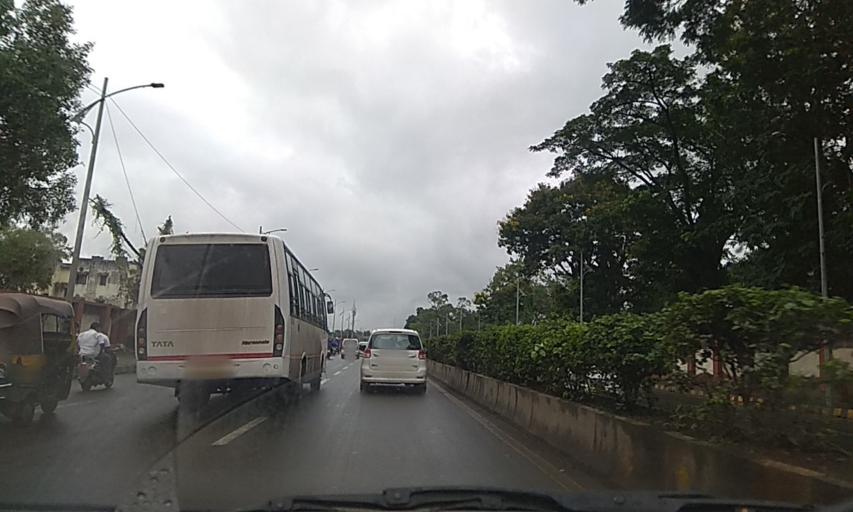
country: IN
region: Maharashtra
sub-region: Pune Division
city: Khadki
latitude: 18.5526
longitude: 73.8651
